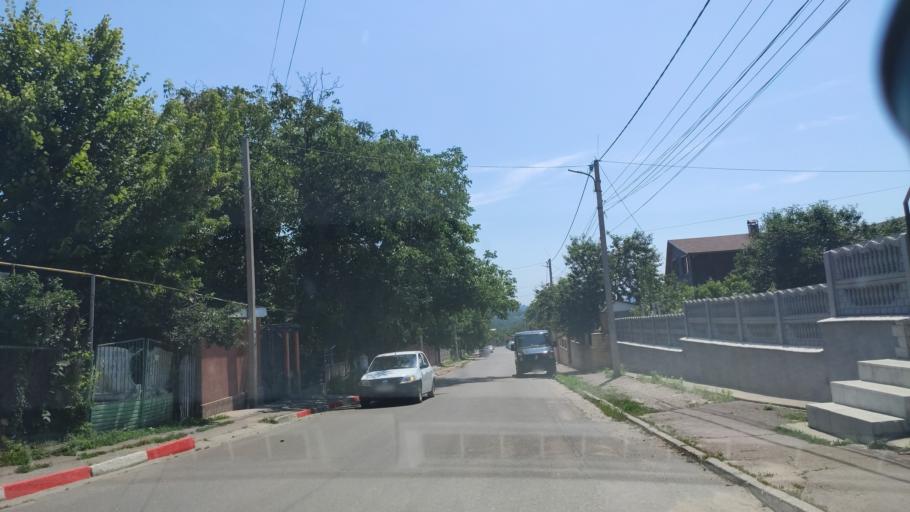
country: MD
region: Raionul Soroca
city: Soroca
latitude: 48.1682
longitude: 28.3010
